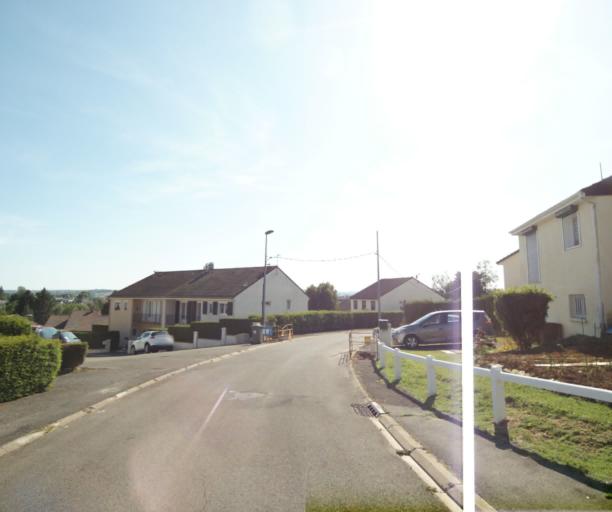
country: FR
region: Champagne-Ardenne
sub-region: Departement des Ardennes
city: Warcq
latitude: 49.7856
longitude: 4.6998
